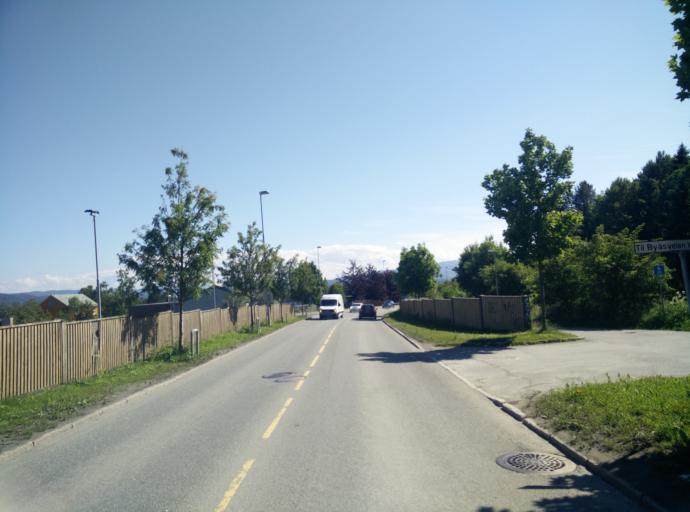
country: NO
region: Sor-Trondelag
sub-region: Trondheim
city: Trondheim
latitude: 63.4003
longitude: 10.3578
